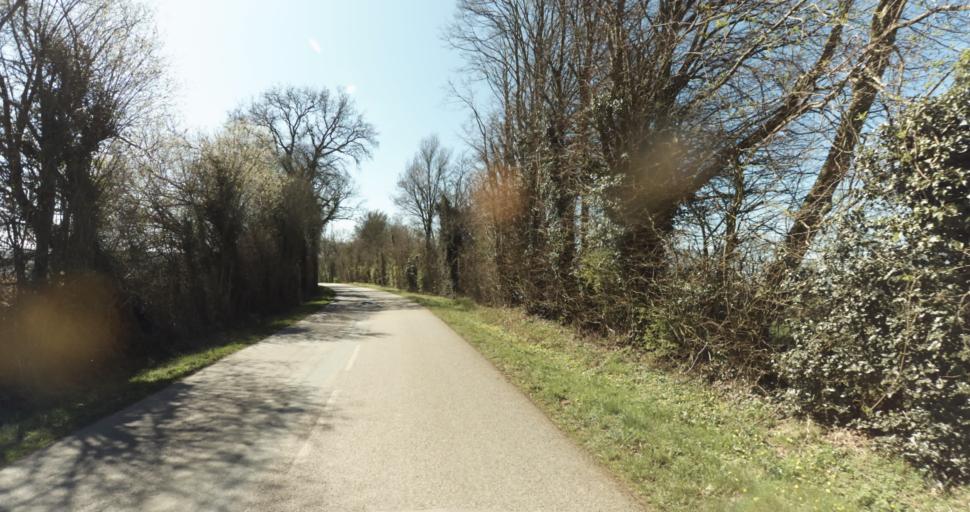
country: FR
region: Lower Normandy
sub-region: Departement de l'Orne
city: Trun
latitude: 48.9100
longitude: 0.0580
